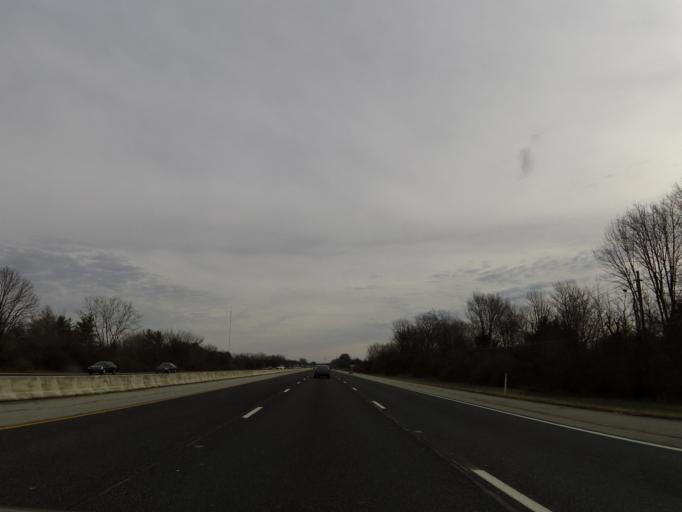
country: US
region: Indiana
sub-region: Boone County
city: Zionsville
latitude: 39.9239
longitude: -86.2108
